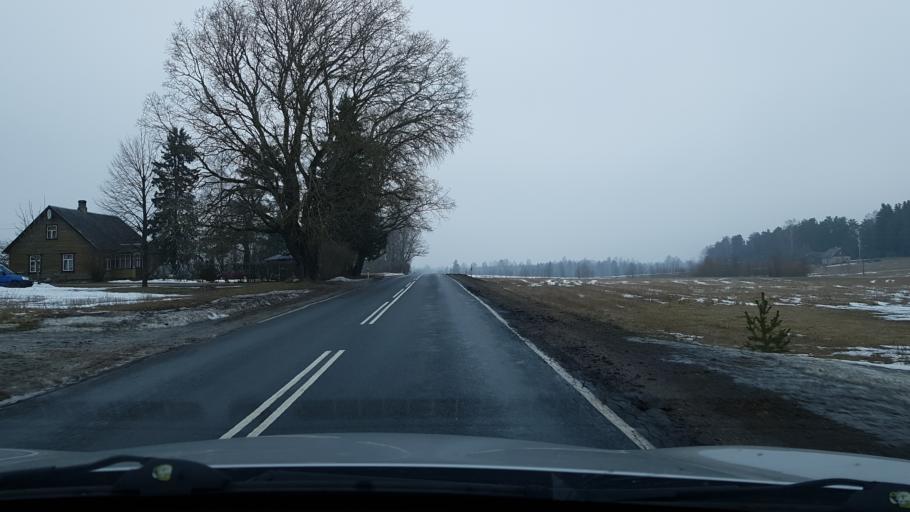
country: EE
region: Valgamaa
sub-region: Torva linn
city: Torva
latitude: 58.1367
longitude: 25.9894
